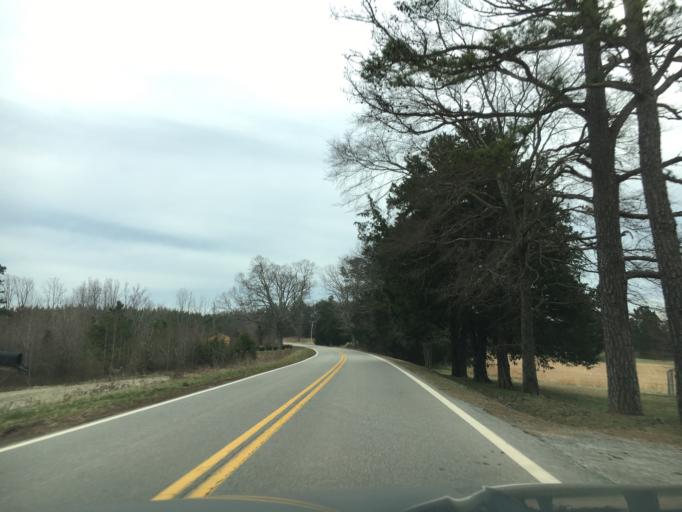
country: US
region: Virginia
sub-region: Charlotte County
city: Charlotte Court House
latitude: 36.9778
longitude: -78.6985
